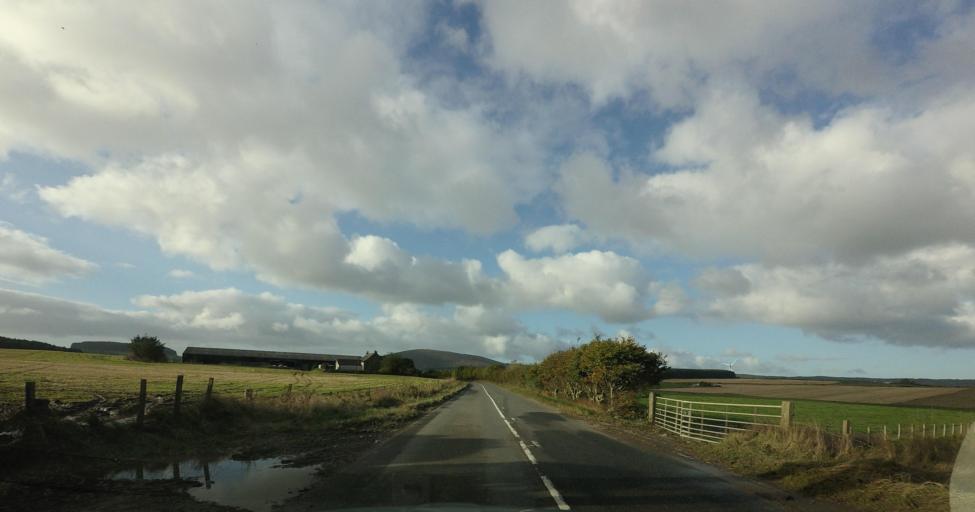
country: GB
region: Scotland
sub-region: Aberdeenshire
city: Portsoy
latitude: 57.6044
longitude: -2.7129
